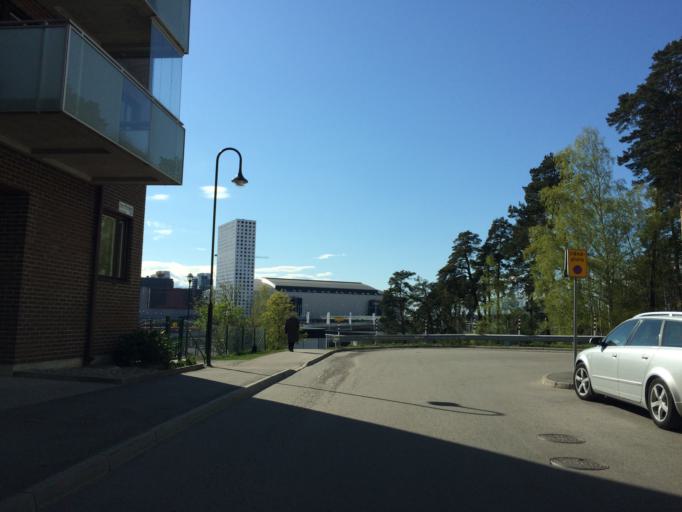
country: SE
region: Stockholm
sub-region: Solna Kommun
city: Solna
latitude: 59.3723
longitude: 18.0120
